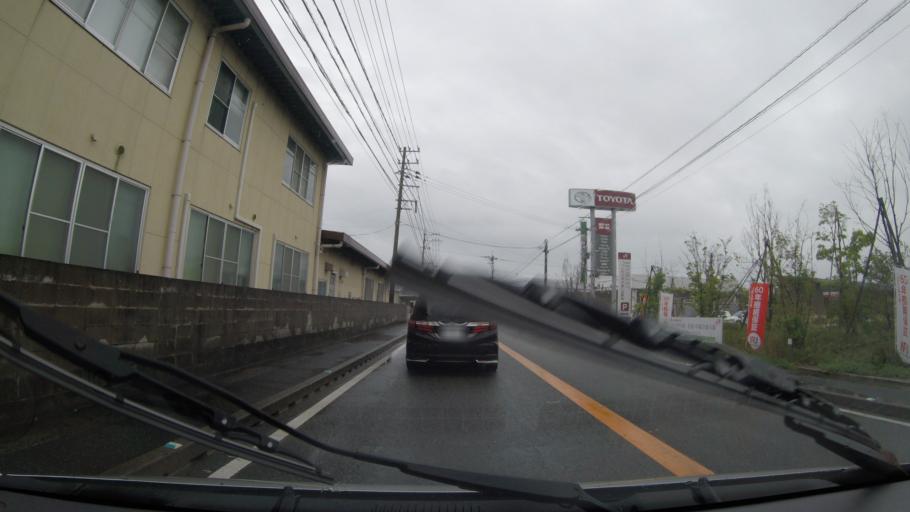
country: JP
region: Fukuoka
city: Koga
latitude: 33.7217
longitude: 130.4557
